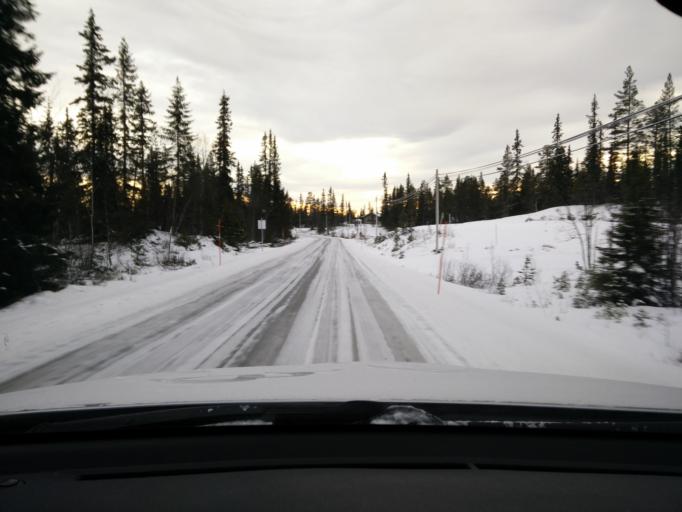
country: SE
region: Jaemtland
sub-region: Bergs Kommun
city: Hoverberg
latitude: 62.4818
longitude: 14.1224
